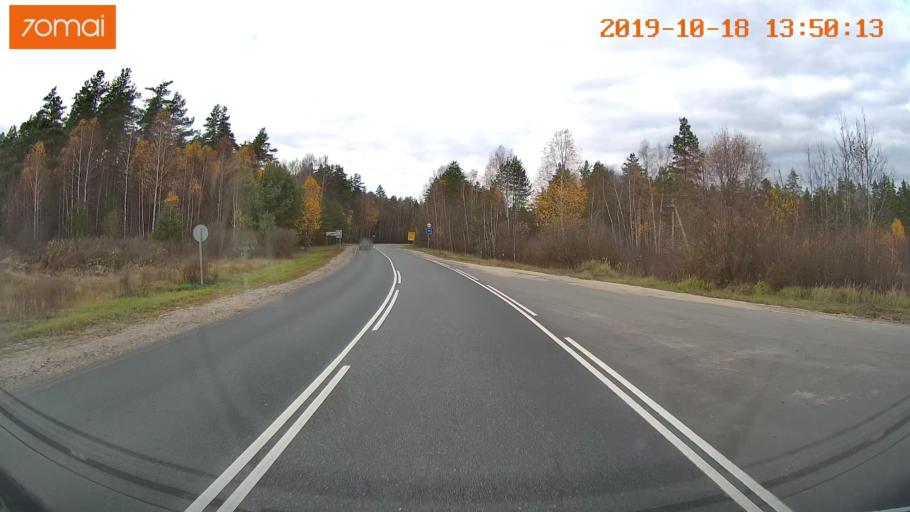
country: RU
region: Moskovskaya
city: Radovitskiy
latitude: 55.0044
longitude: 39.9741
